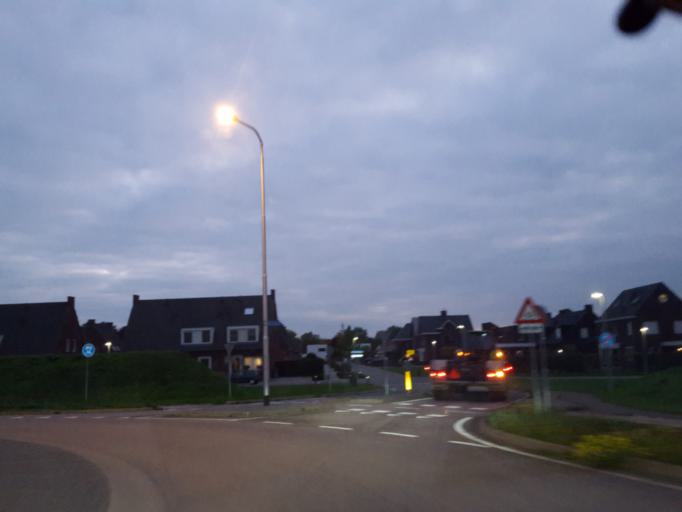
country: NL
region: Limburg
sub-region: Gemeente Nederweert
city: Nederweert
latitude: 51.2925
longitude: 5.7526
